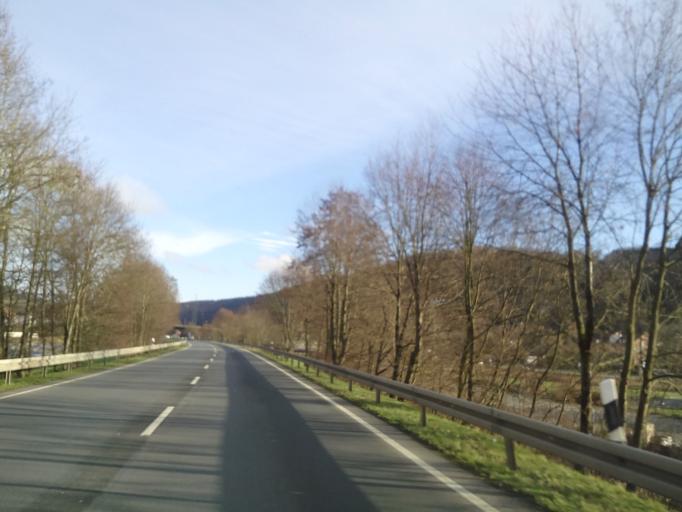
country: DE
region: Bavaria
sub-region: Upper Franconia
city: Kulmbach
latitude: 50.1129
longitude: 11.4596
